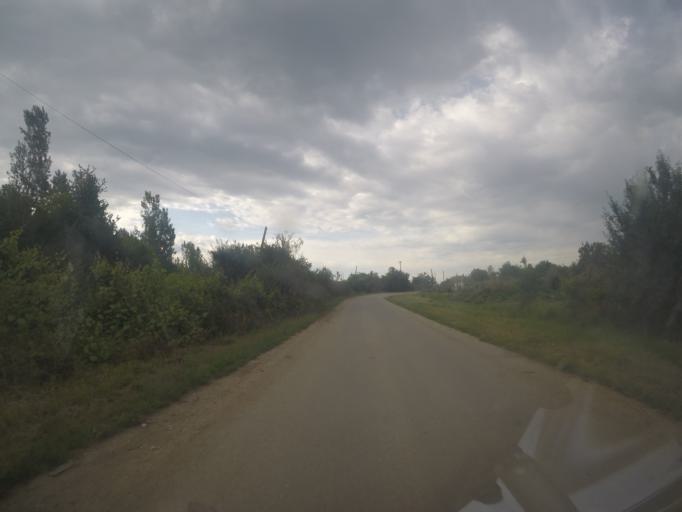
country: RS
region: Central Serbia
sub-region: Belgrade
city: Zemun
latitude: 44.9040
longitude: 20.4221
